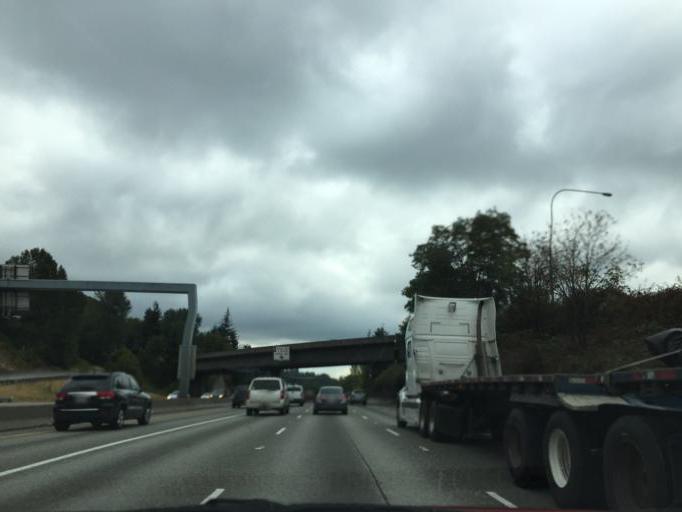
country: US
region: Washington
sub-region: King County
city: Riverton
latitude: 47.5003
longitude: -122.2749
